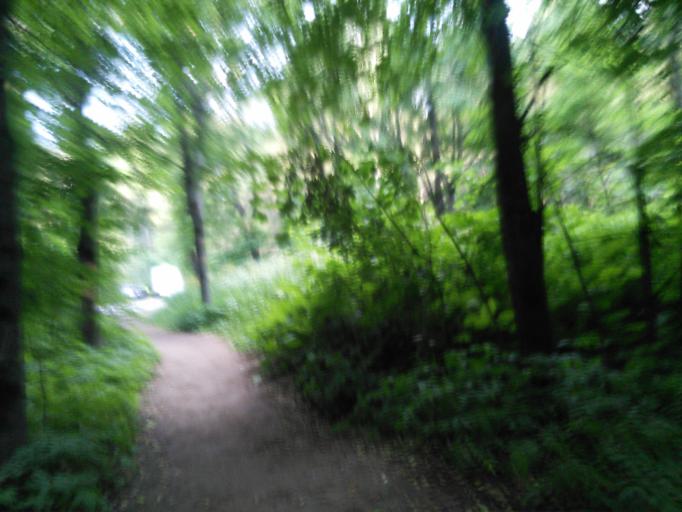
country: RU
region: Moscow
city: Sokol'niki
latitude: 55.8081
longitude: 37.6741
